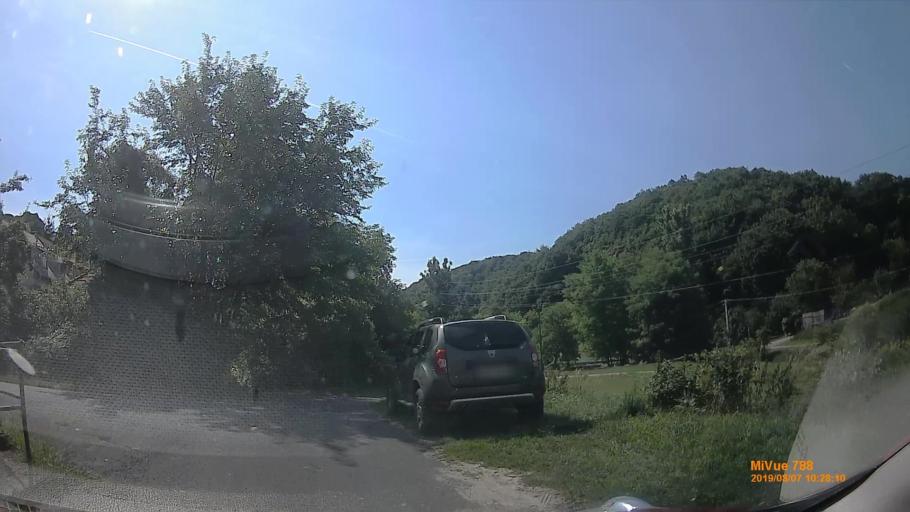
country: HU
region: Veszprem
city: Ajka
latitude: 47.0854
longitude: 17.5721
